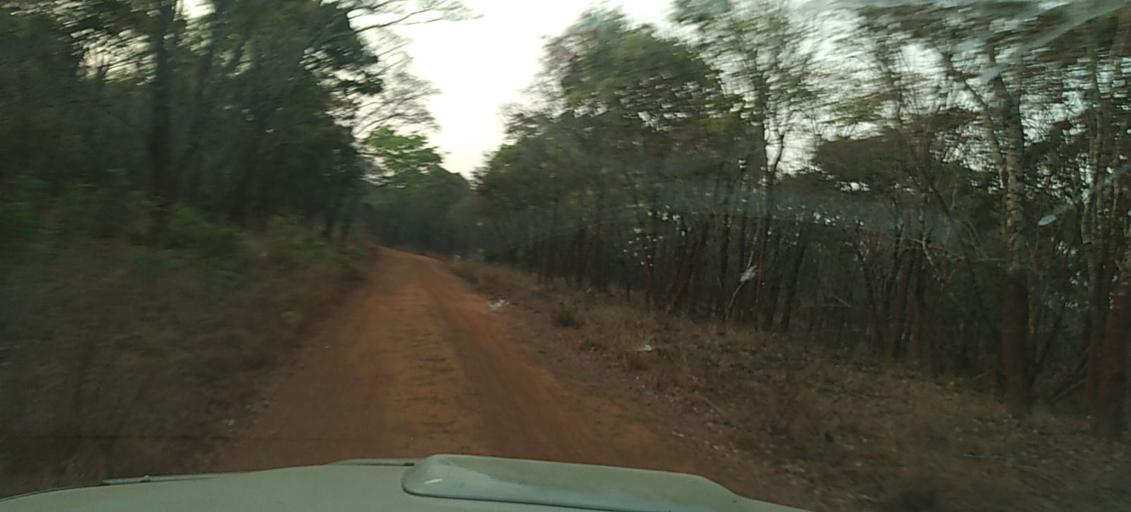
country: ZM
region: North-Western
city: Kasempa
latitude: -13.0871
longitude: 26.3979
